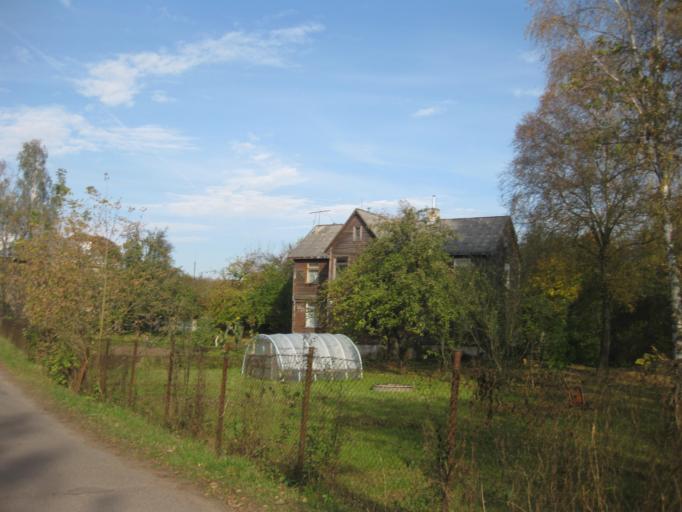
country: LT
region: Kauno apskritis
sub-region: Kaunas
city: Aleksotas
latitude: 54.8890
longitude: 23.8870
